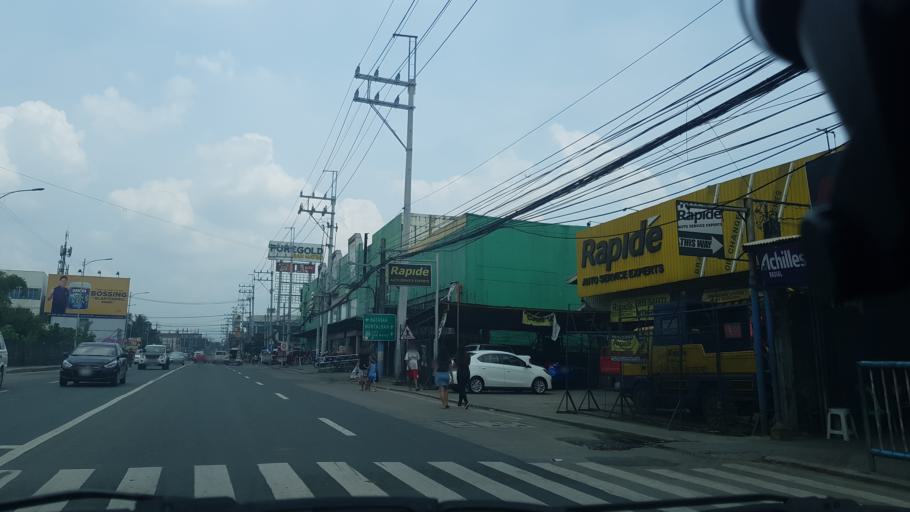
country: PH
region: Calabarzon
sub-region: Province of Rizal
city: San Mateo
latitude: 14.6765
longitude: 121.1107
